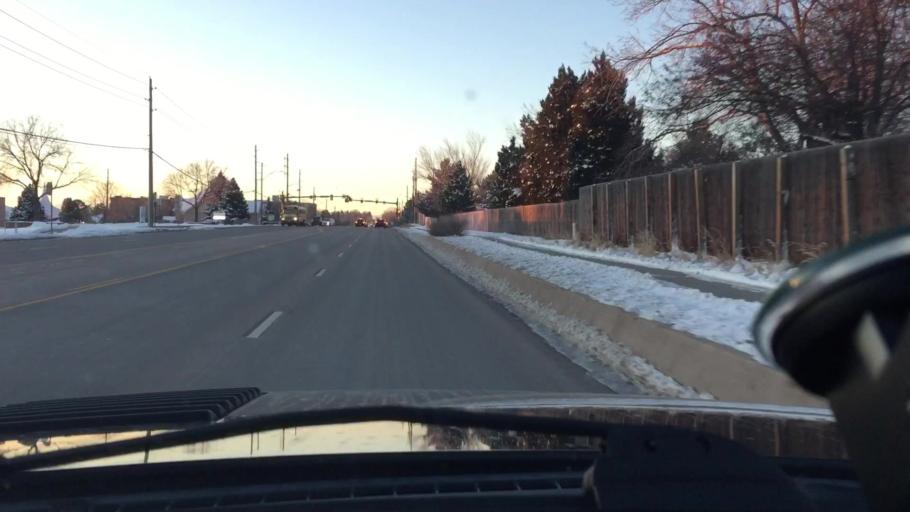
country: US
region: Colorado
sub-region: Adams County
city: Northglenn
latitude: 39.8950
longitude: -104.9968
